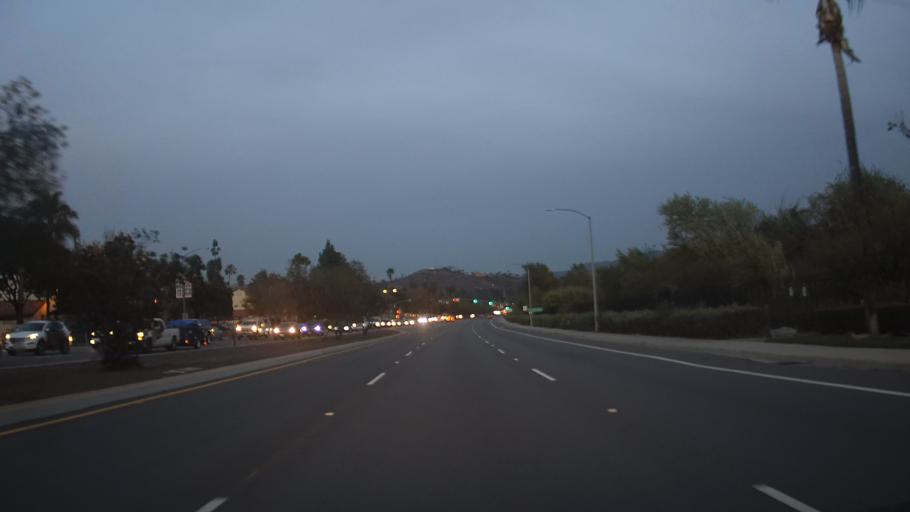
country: US
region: California
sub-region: San Diego County
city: Rancho San Diego
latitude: 32.7418
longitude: -116.9369
